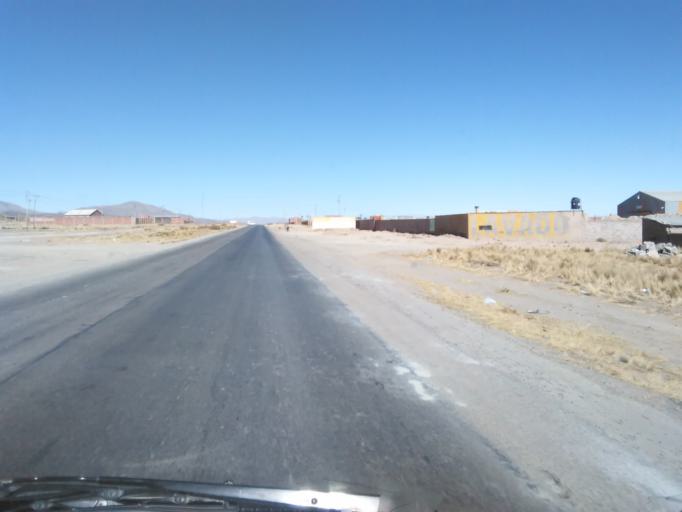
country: BO
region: Oruro
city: Oruro
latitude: -17.9938
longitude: -67.0465
